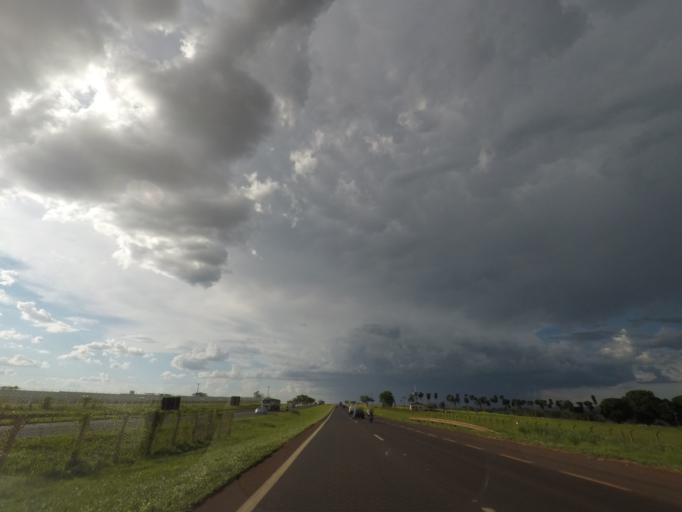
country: BR
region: Sao Paulo
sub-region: Ribeirao Preto
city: Ribeirao Preto
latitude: -21.0971
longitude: -47.7914
